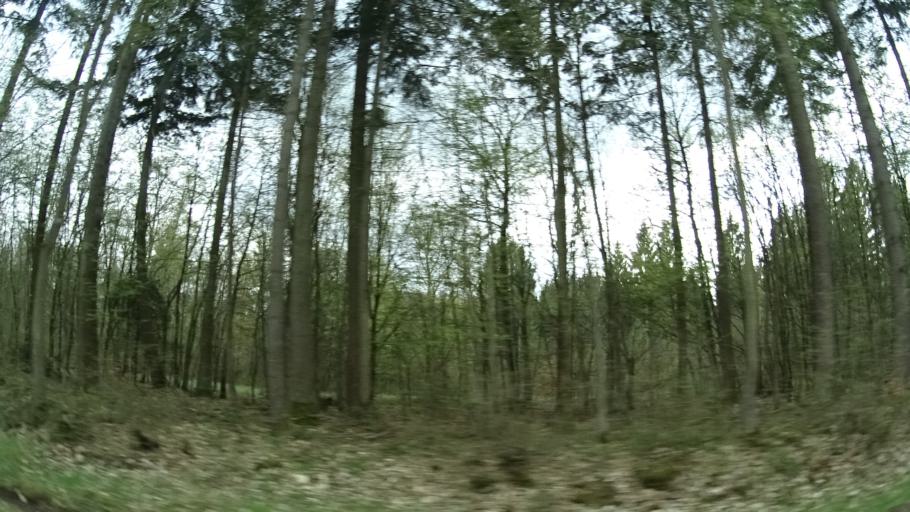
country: DE
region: Rheinland-Pfalz
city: Seesbach
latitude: 49.8667
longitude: 7.5726
